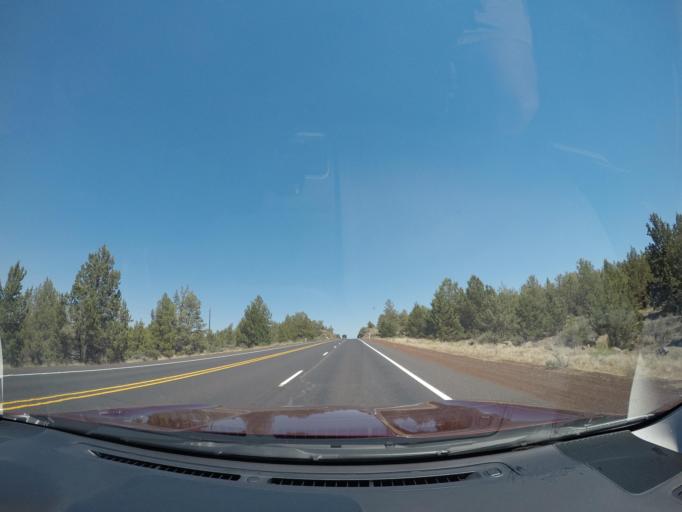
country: US
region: Oregon
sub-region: Deschutes County
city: Sisters
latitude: 44.2948
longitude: -121.3934
